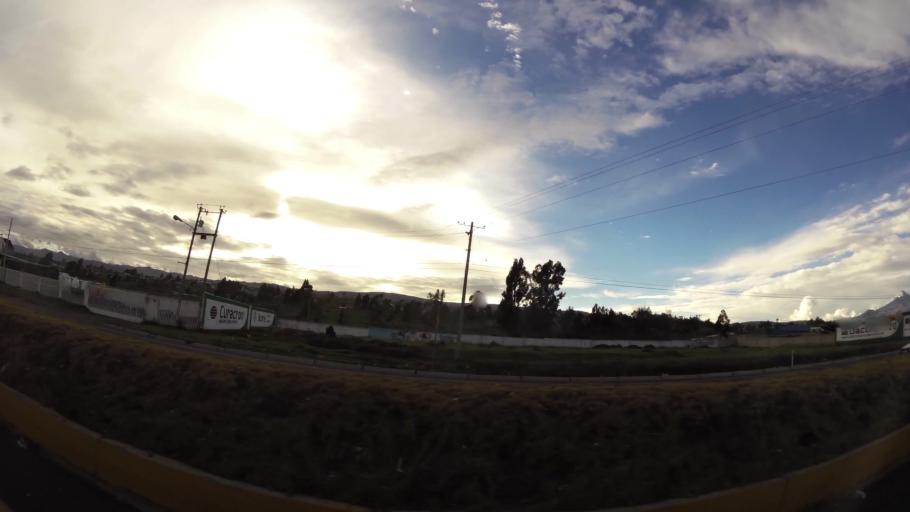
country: EC
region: Cotopaxi
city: Latacunga
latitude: -0.8974
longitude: -78.6287
